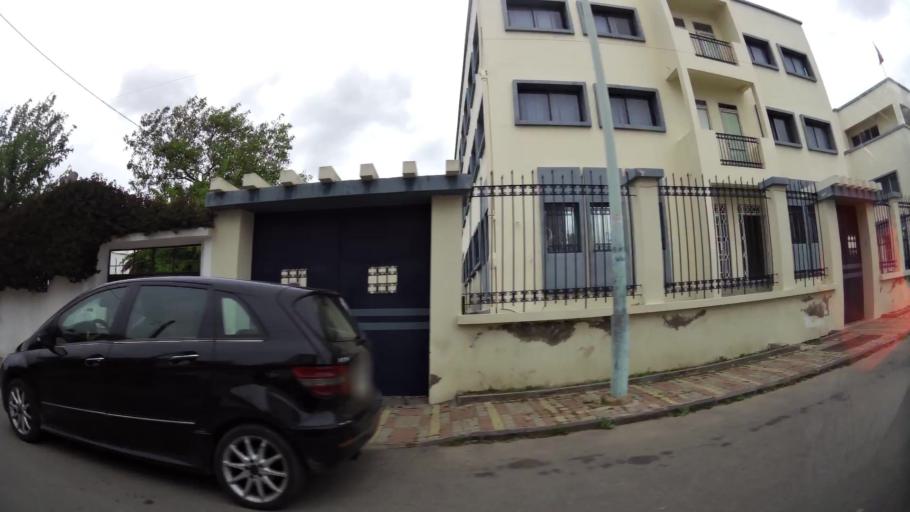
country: MA
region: Grand Casablanca
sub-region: Casablanca
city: Casablanca
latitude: 33.5654
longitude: -7.6241
